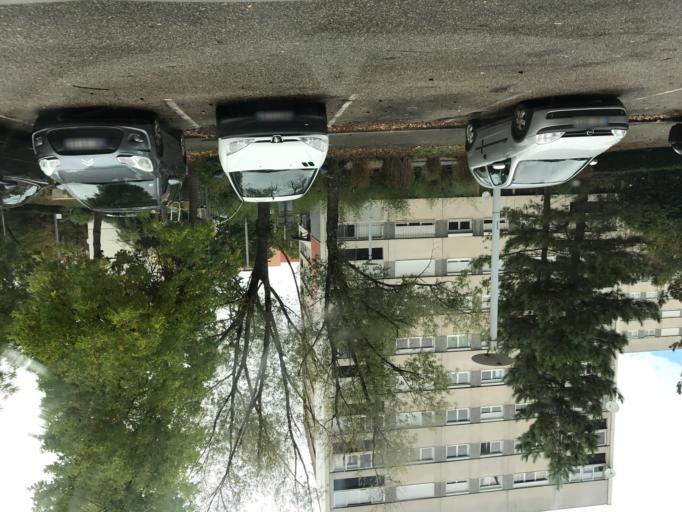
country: FR
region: Rhone-Alpes
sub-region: Departement du Rhone
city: Rillieux-la-Pape
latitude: 45.8125
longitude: 4.9046
